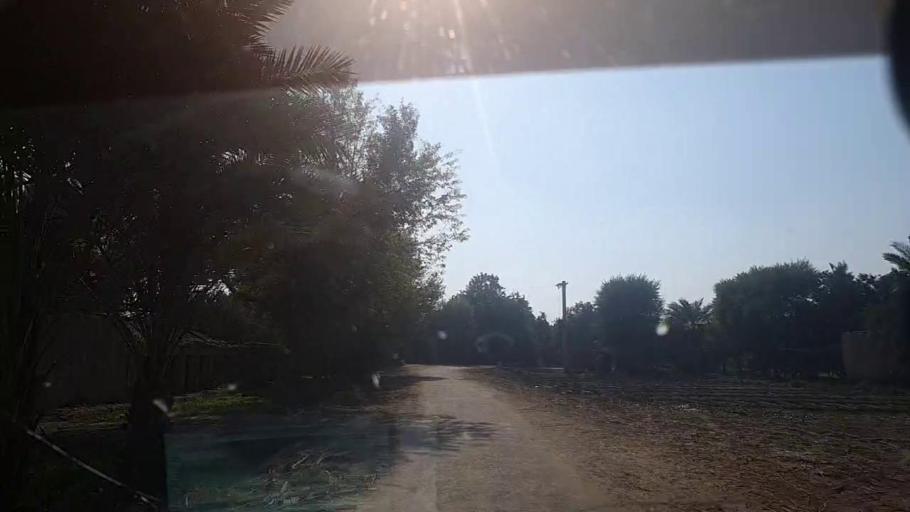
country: PK
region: Sindh
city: Gambat
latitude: 27.3880
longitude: 68.5991
